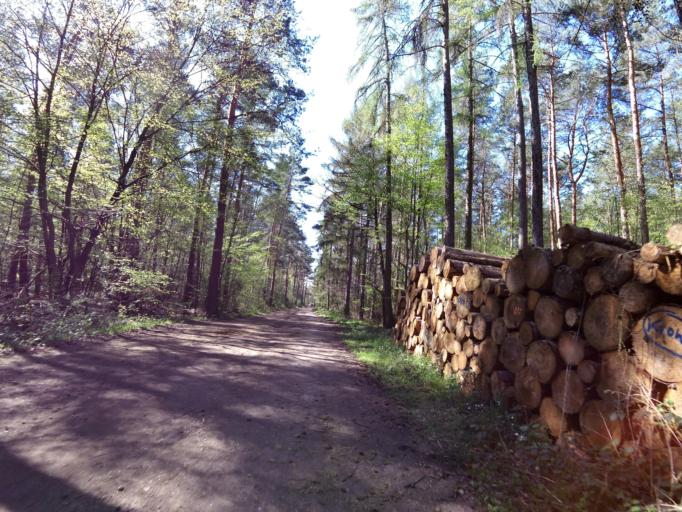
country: DE
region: North Rhine-Westphalia
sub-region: Regierungsbezirk Koln
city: Alfter
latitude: 50.6816
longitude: 6.9918
